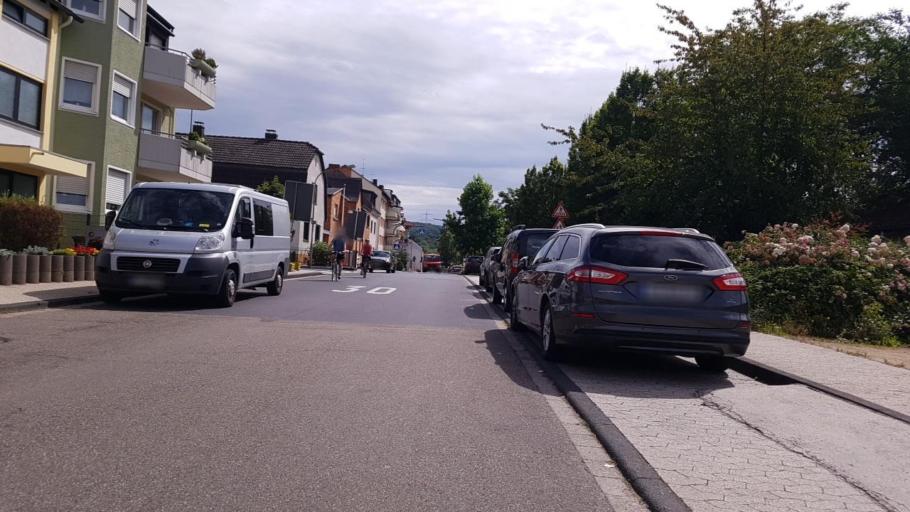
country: DE
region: Rheinland-Pfalz
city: Niederwerth
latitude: 50.3831
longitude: 7.6046
